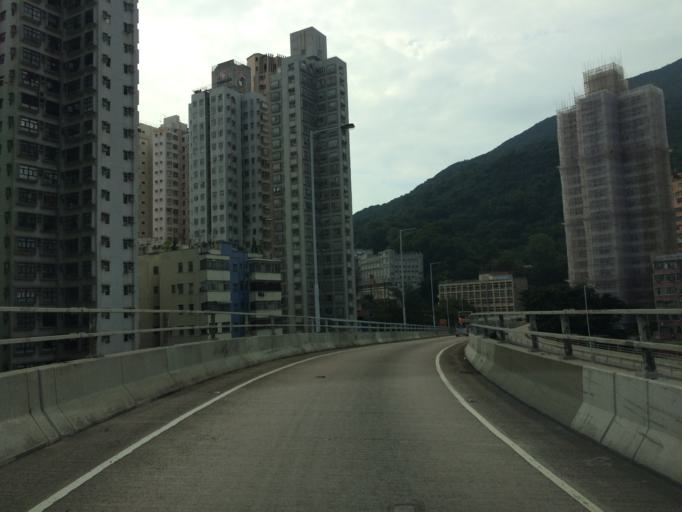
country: HK
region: Wanchai
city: Wan Chai
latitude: 22.2791
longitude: 114.2280
